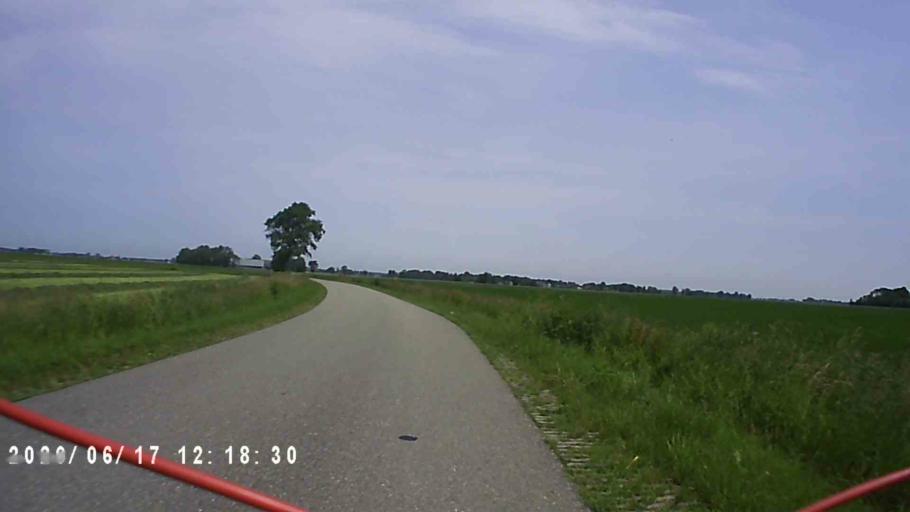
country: NL
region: Groningen
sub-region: Gemeente Zuidhorn
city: Oldehove
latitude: 53.3316
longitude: 6.4153
